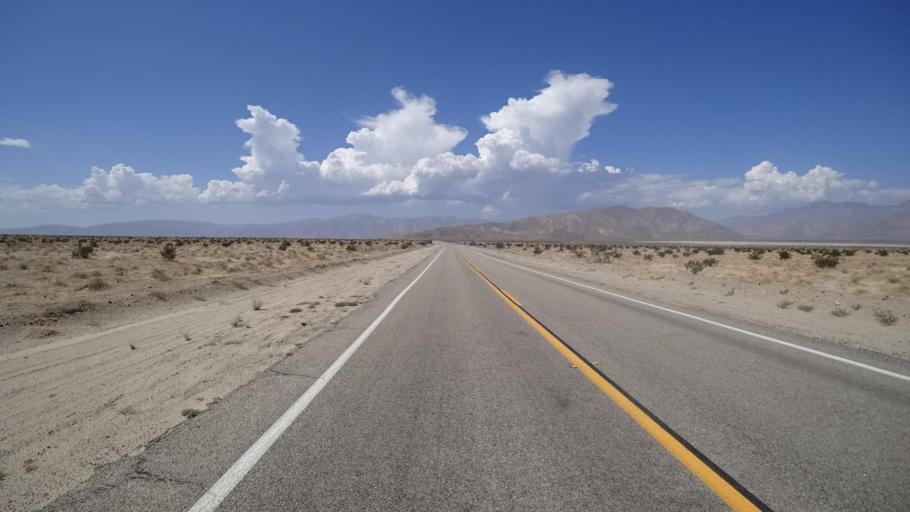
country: US
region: California
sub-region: San Diego County
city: Borrego Springs
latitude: 33.3036
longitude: -116.2435
